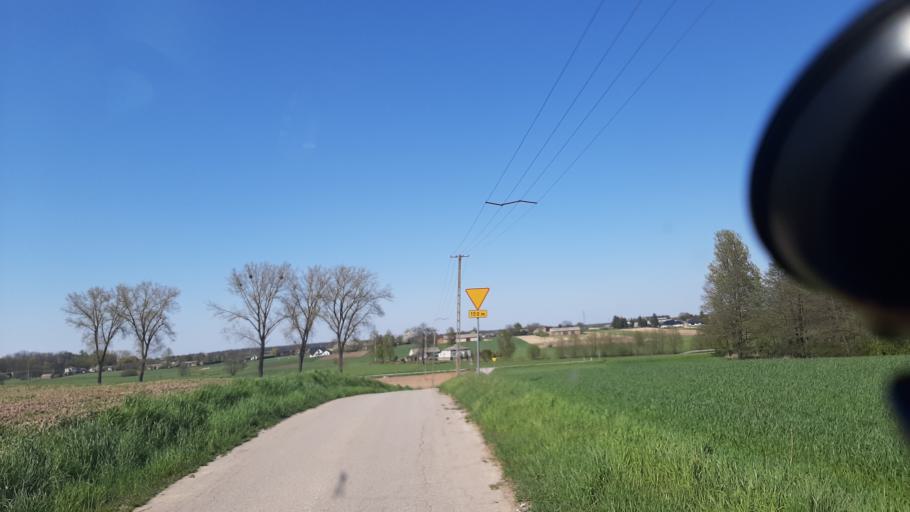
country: PL
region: Lublin Voivodeship
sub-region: Powiat lubelski
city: Jastkow
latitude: 51.3432
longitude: 22.3931
